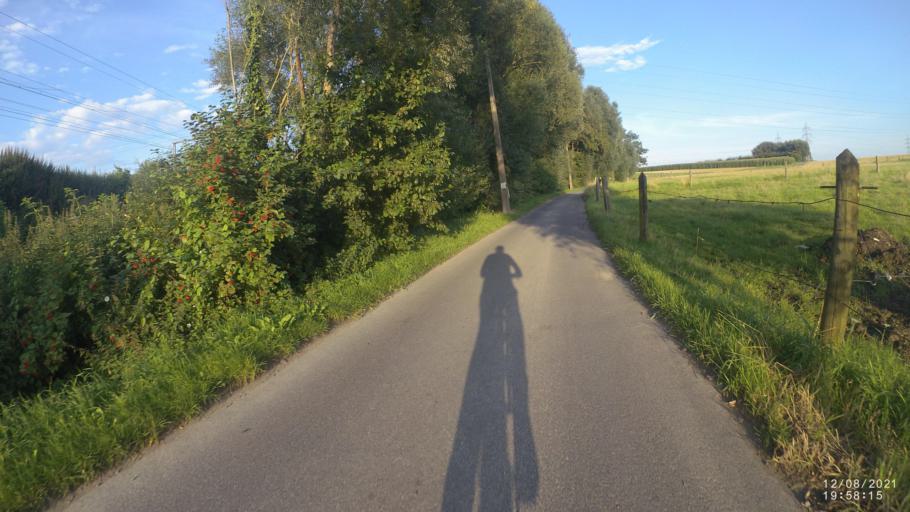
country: BE
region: Flanders
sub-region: Provincie Vlaams-Brabant
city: Dilbeek
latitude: 50.8684
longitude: 4.2277
